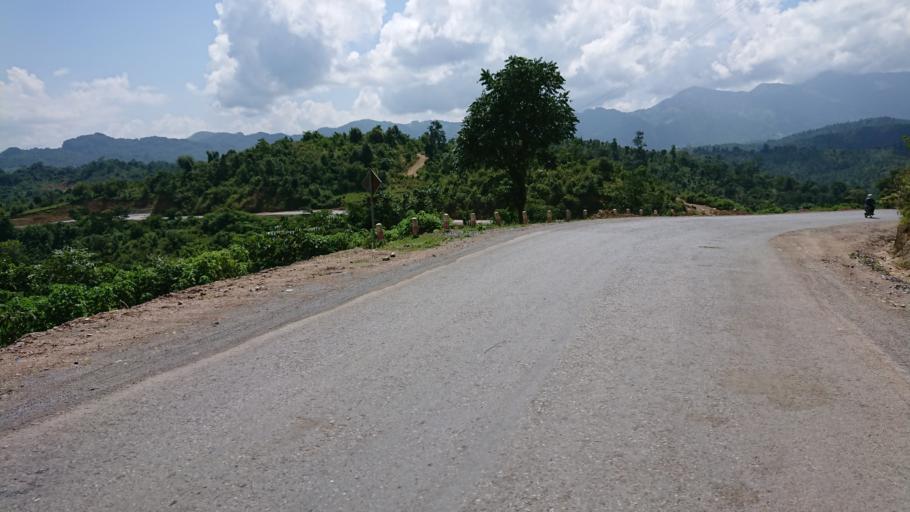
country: MM
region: Shan
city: Taunggyi
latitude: 20.8168
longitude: 97.3076
